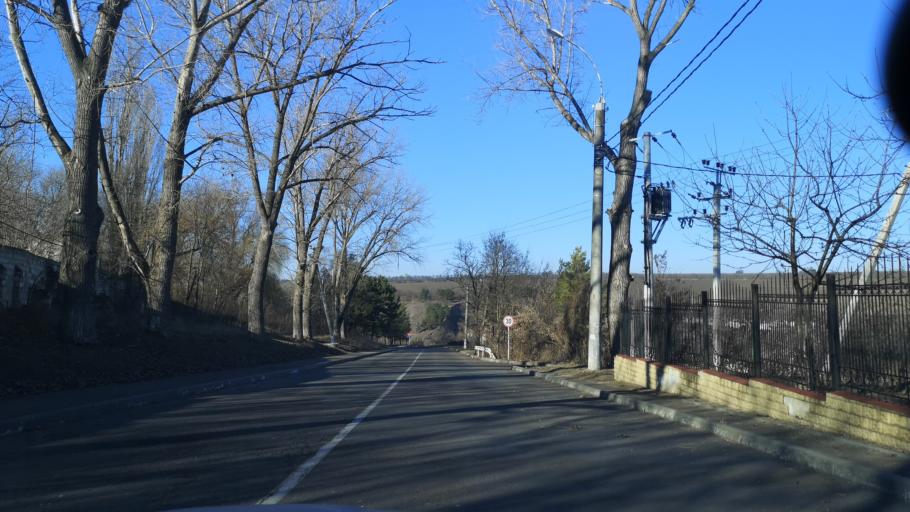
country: MD
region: Chisinau
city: Cricova
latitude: 47.1455
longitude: 28.8635
